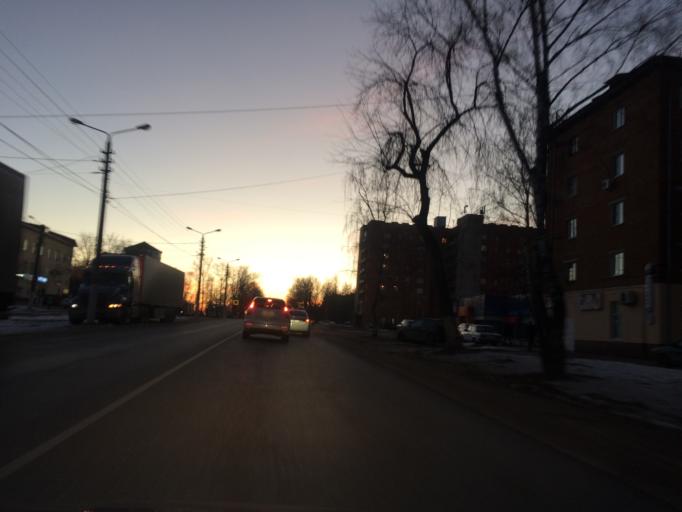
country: RU
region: Tula
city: Tula
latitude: 54.2139
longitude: 37.6682
